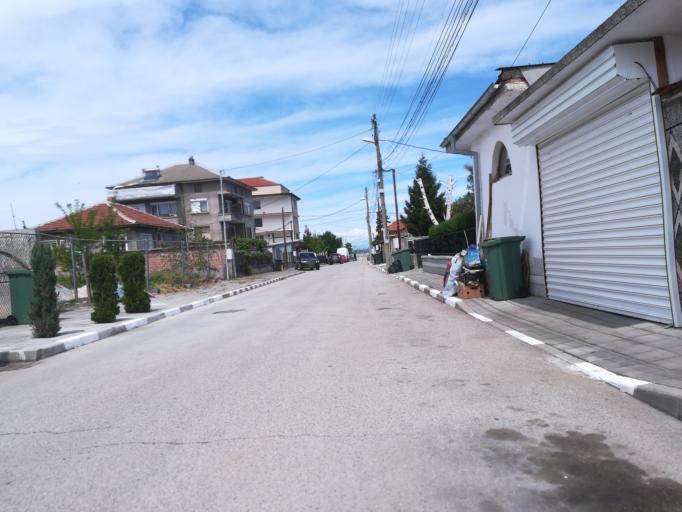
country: BG
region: Stara Zagora
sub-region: Obshtina Chirpan
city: Chirpan
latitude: 42.0974
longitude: 25.2175
